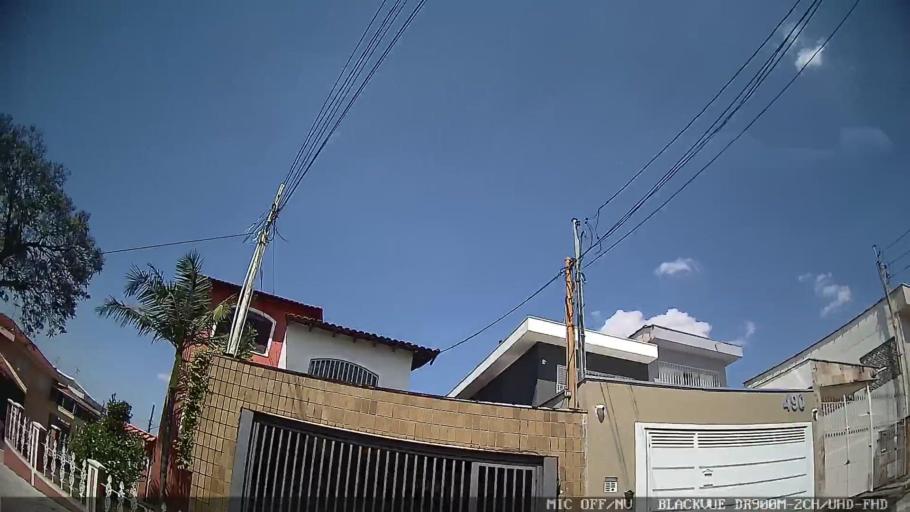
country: BR
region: Sao Paulo
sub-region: Guarulhos
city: Guarulhos
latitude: -23.5013
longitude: -46.5201
